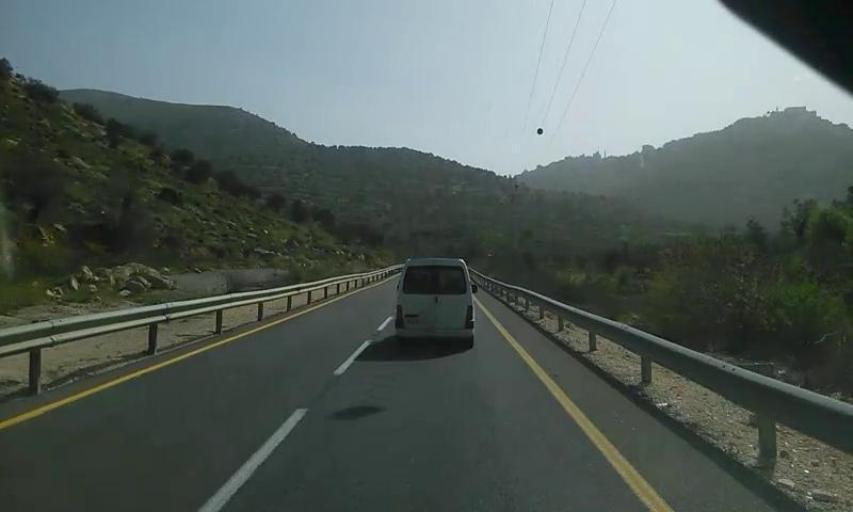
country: PS
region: West Bank
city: Silwad
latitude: 31.9942
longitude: 35.2479
